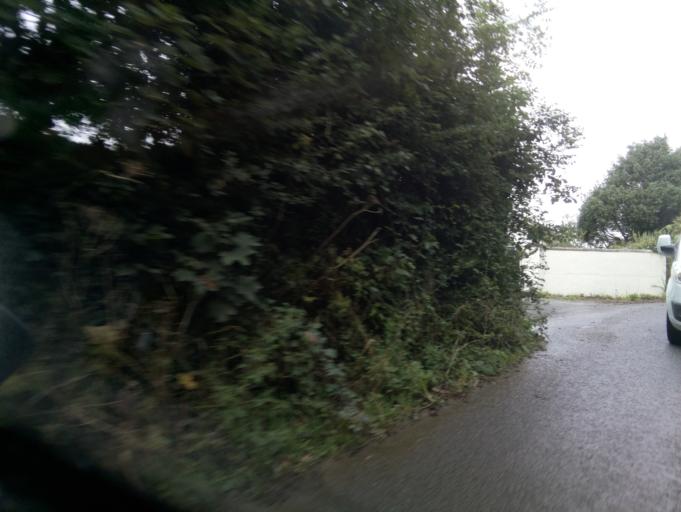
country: GB
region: England
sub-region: Devon
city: Kingsbridge
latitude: 50.2690
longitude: -3.8239
